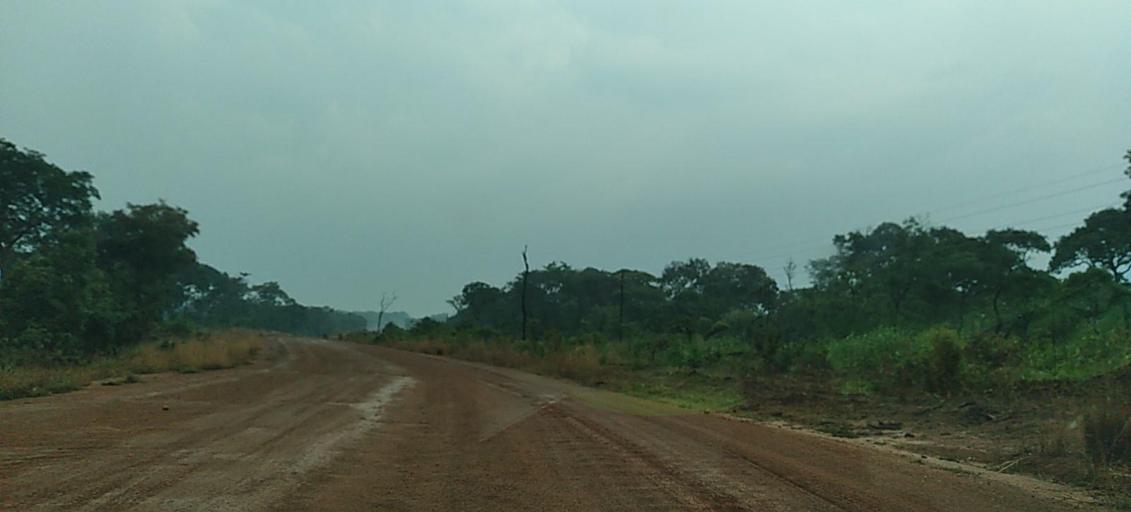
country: ZM
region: North-Western
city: Mwinilunga
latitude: -11.5897
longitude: 24.3872
